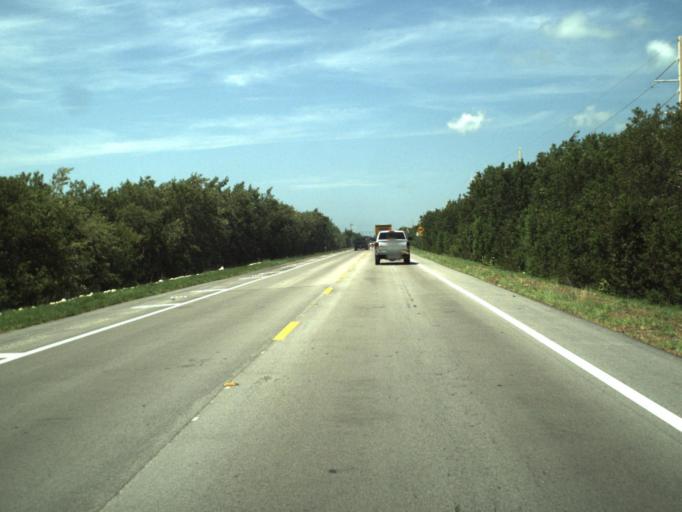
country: US
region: Florida
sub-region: Monroe County
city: Marathon
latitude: 24.7500
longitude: -80.9740
